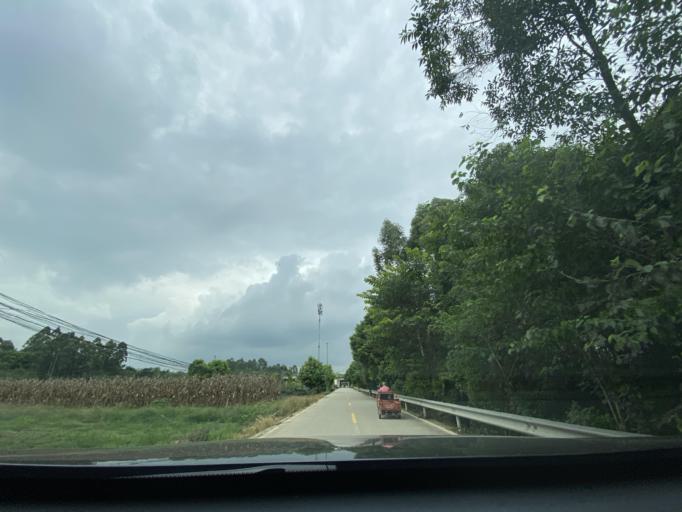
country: CN
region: Sichuan
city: Wujin
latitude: 30.3836
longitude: 103.9676
